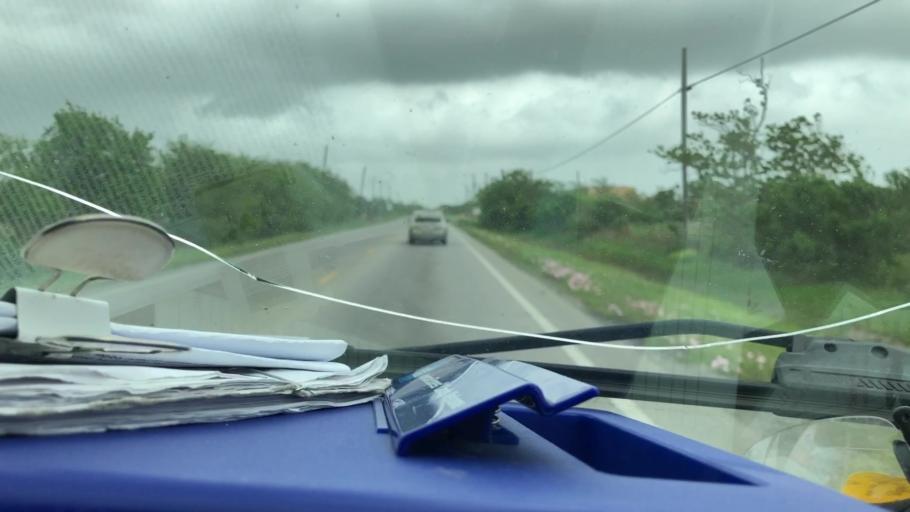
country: US
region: Texas
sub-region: Galveston County
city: Bacliff
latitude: 29.4749
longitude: -94.9717
